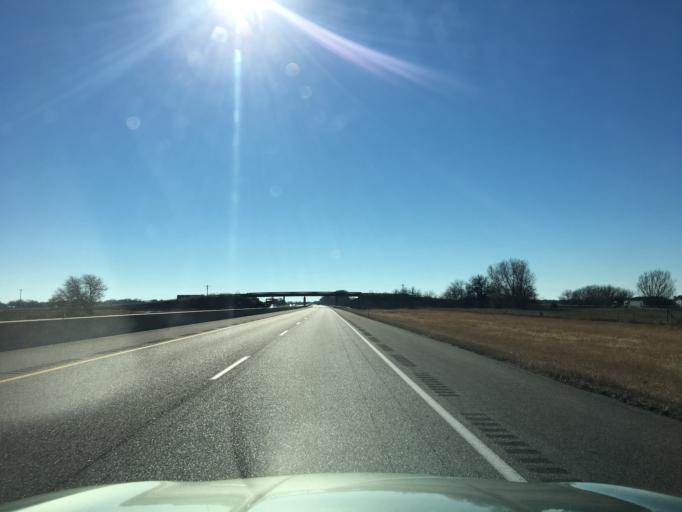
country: US
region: Kansas
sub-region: Sumner County
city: Belle Plaine
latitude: 37.4527
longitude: -97.3223
